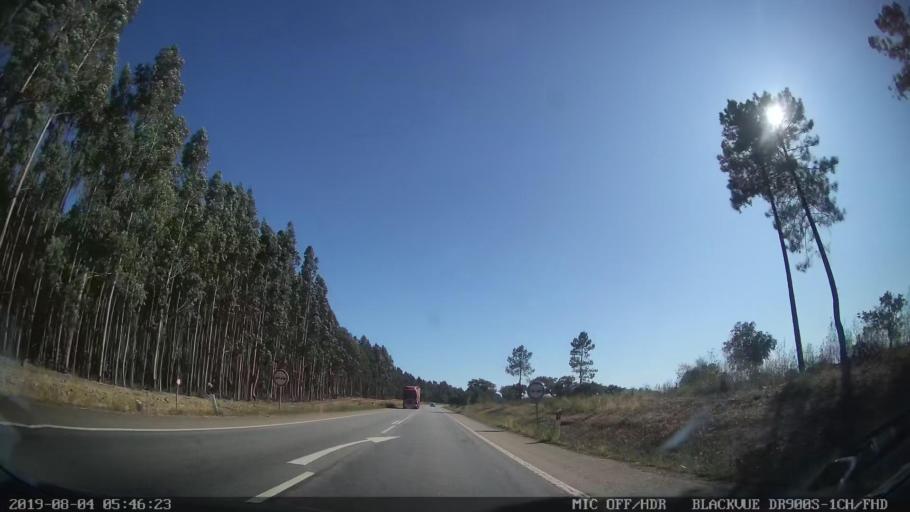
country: PT
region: Portalegre
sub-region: Gaviao
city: Gaviao
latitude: 39.4514
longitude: -7.7875
